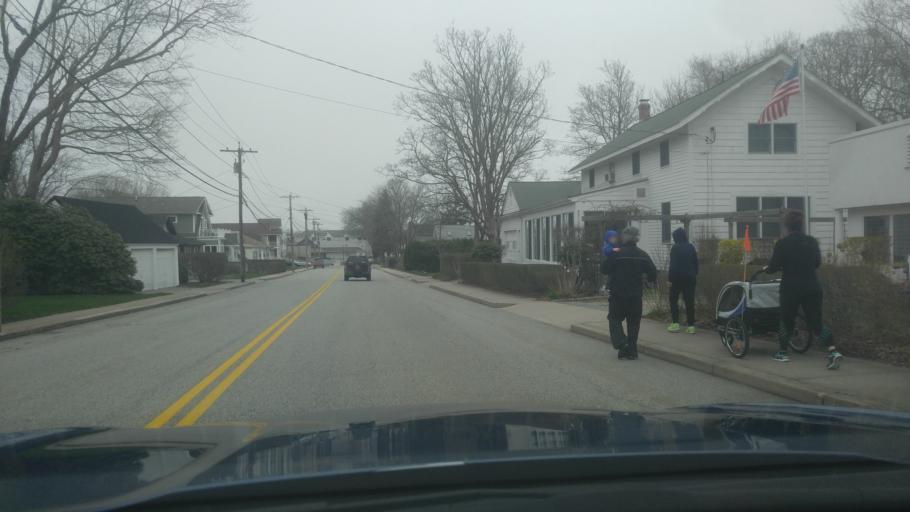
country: US
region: Rhode Island
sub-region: Washington County
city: Narragansett Pier
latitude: 41.4289
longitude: -71.4587
